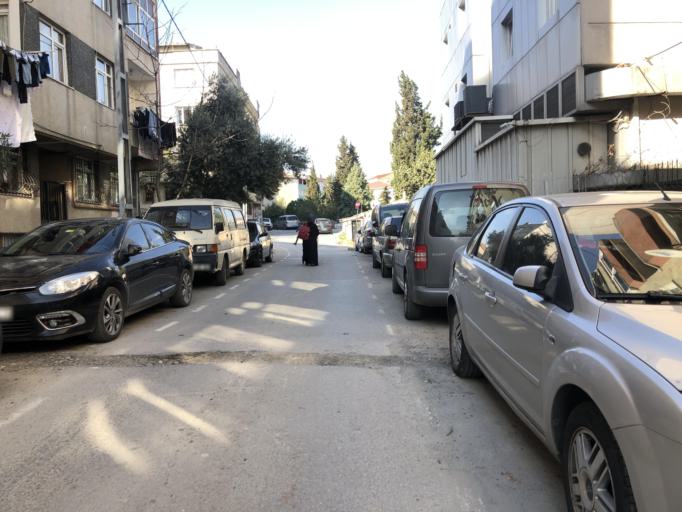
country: TR
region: Istanbul
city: Esenler
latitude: 41.0712
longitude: 28.9009
